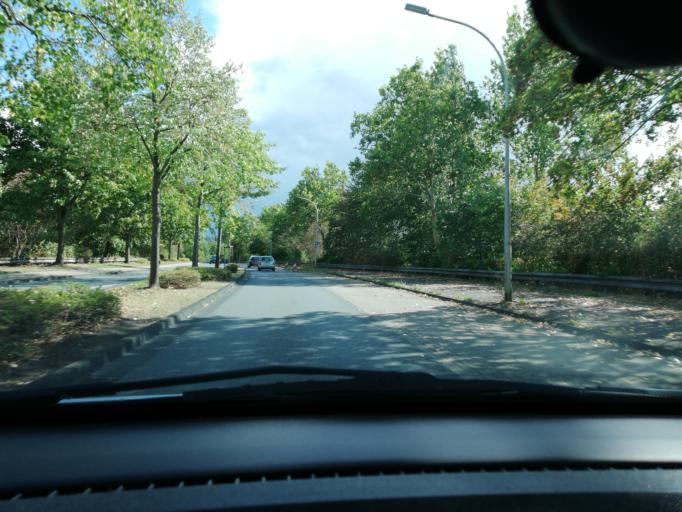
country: DE
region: North Rhine-Westphalia
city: Witten
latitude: 51.4534
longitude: 7.3921
